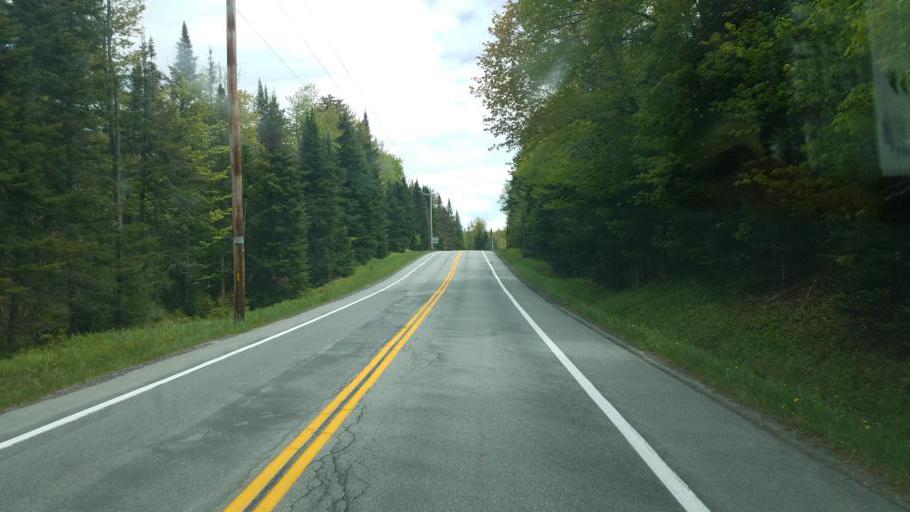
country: US
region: New York
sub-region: Hamilton County
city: Lake Pleasant
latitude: 43.8058
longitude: -74.6684
